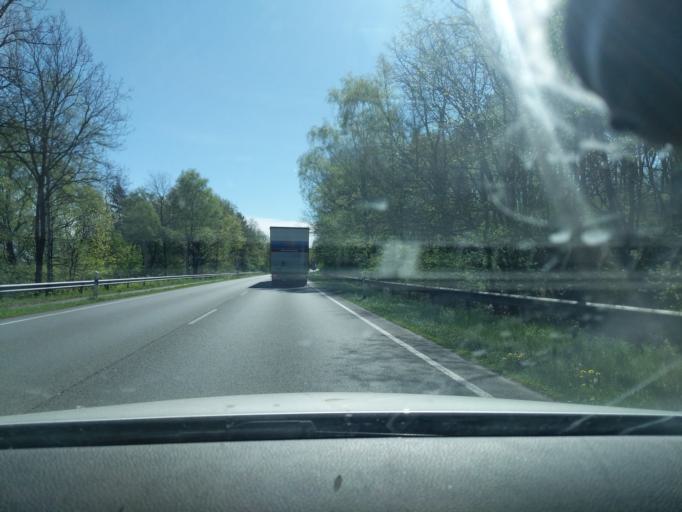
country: DE
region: Lower Saxony
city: Buxtehude
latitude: 53.4608
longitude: 9.7149
